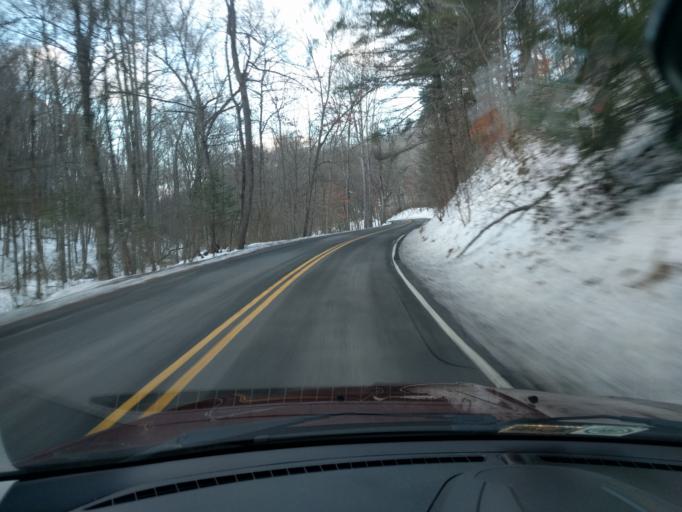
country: US
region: Virginia
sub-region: Bath County
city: Warm Springs
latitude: 38.0913
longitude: -79.8587
